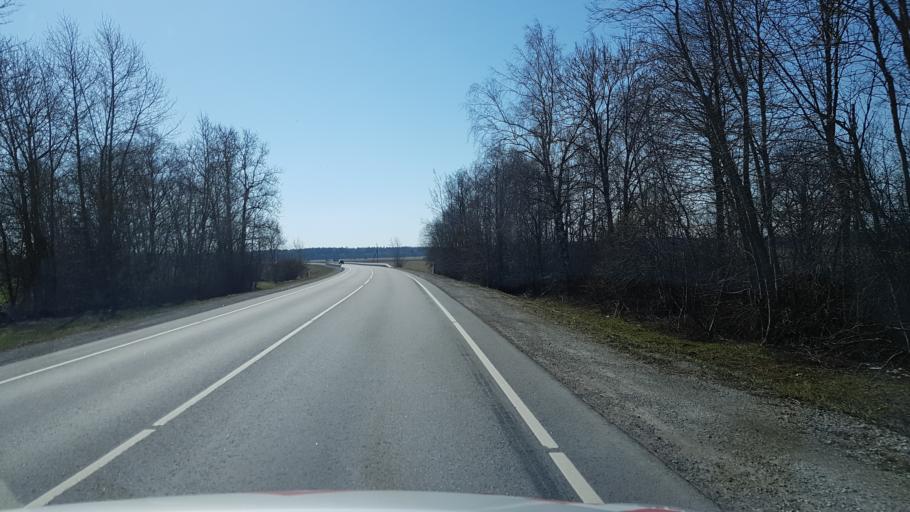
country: EE
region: Ida-Virumaa
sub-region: Kohtla-Jaerve linn
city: Kohtla-Jarve
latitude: 59.3496
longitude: 27.2421
